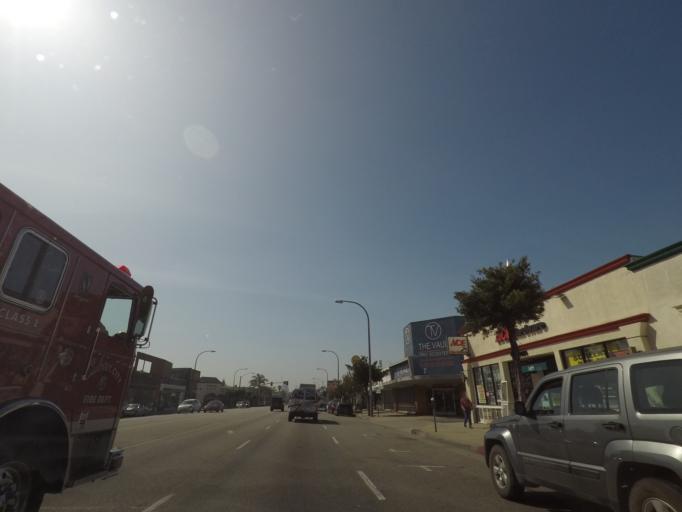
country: US
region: California
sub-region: Los Angeles County
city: Ladera Heights
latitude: 33.9942
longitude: -118.3954
